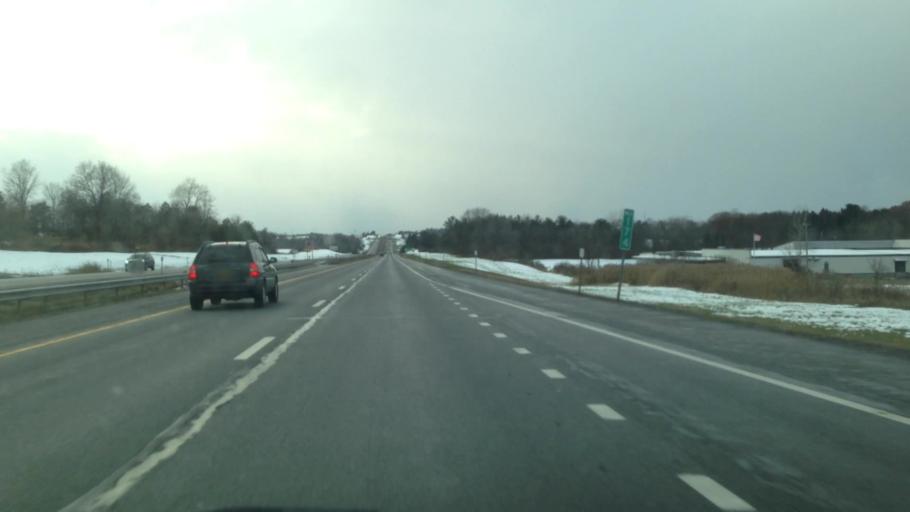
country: US
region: New York
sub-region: Montgomery County
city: Amsterdam
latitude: 42.9247
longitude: -74.2043
